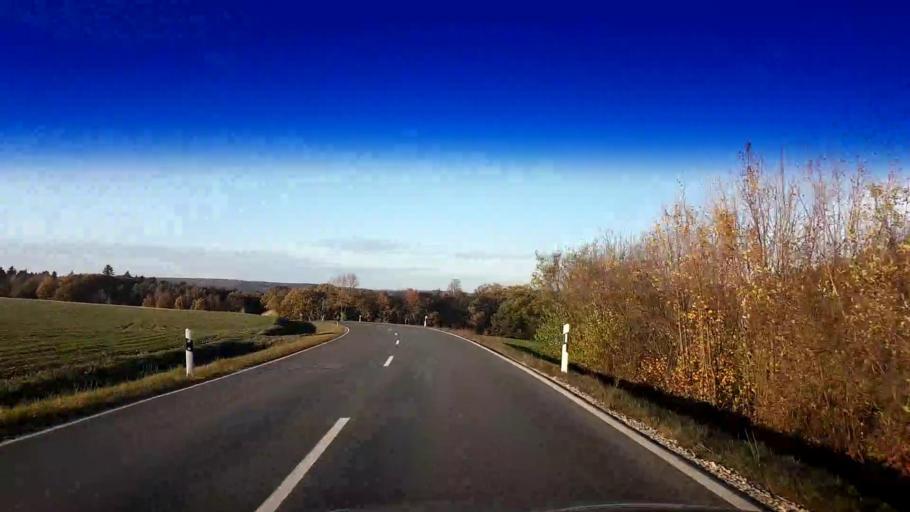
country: DE
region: Bavaria
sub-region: Upper Franconia
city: Zapfendorf
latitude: 50.0058
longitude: 10.9510
